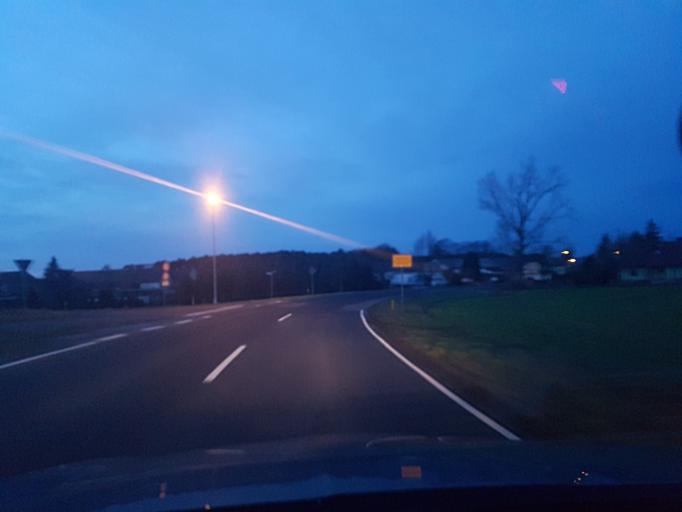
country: DE
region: Brandenburg
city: Trobitz
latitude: 51.5572
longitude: 13.4181
